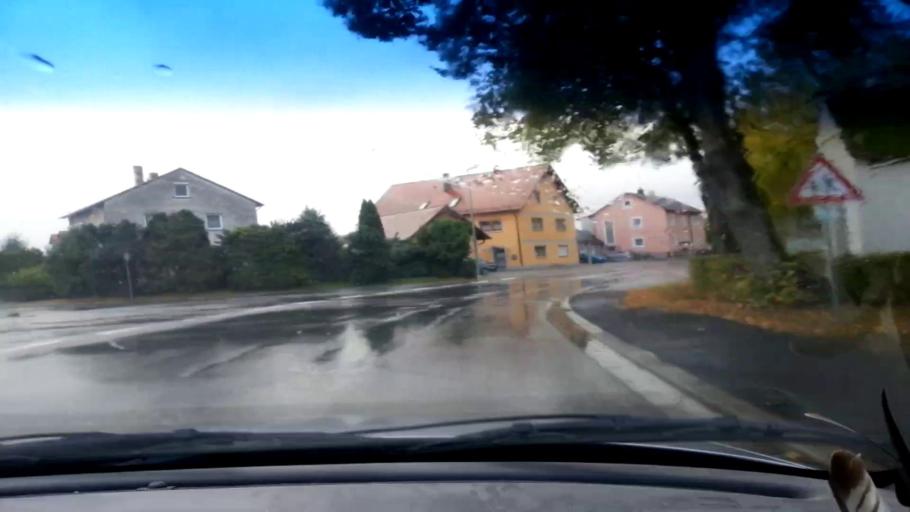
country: DE
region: Bavaria
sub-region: Upper Franconia
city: Burgebrach
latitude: 49.8484
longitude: 10.7330
